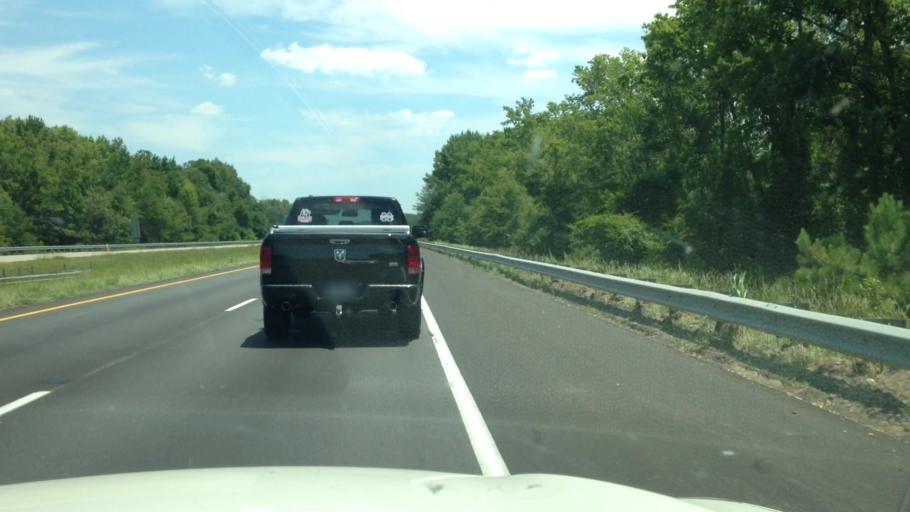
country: US
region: South Carolina
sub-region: Lee County
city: Bishopville
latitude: 34.1882
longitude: -80.1816
